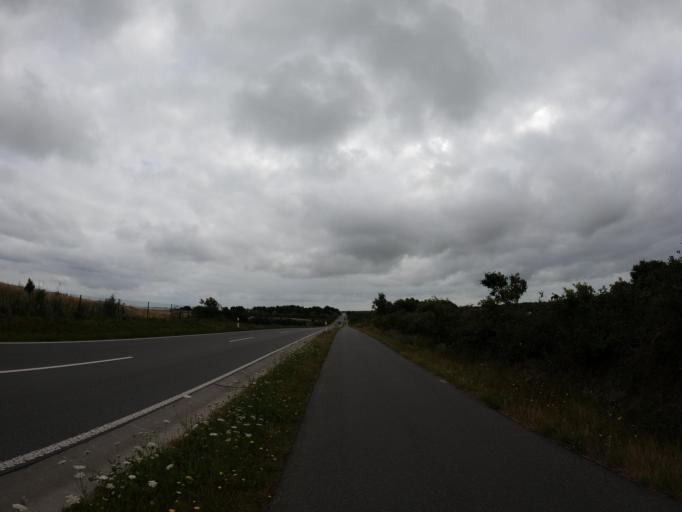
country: DE
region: Schleswig-Holstein
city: Tinnum
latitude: 54.9260
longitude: 8.3574
